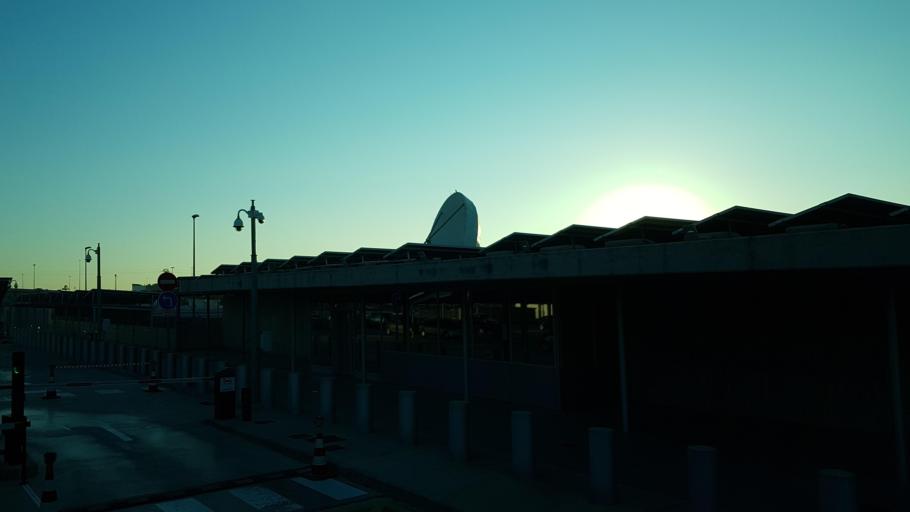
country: ES
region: Valencia
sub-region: Provincia de Valencia
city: Manises
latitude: 39.4783
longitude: -0.4857
